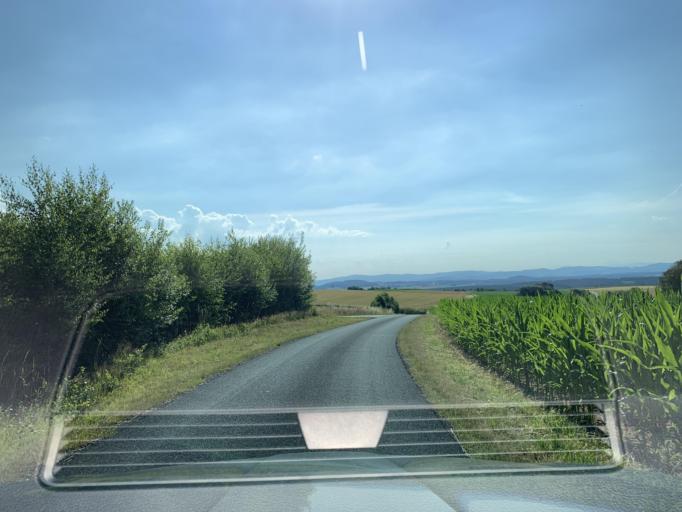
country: DE
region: Bavaria
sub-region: Upper Palatinate
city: Dieterskirchen
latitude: 49.4101
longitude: 12.4466
